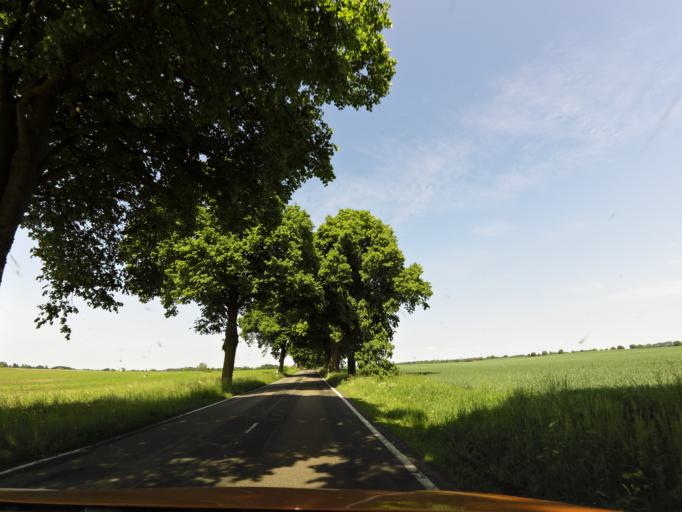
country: DE
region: Mecklenburg-Vorpommern
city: Parchim
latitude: 53.4174
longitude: 11.8806
